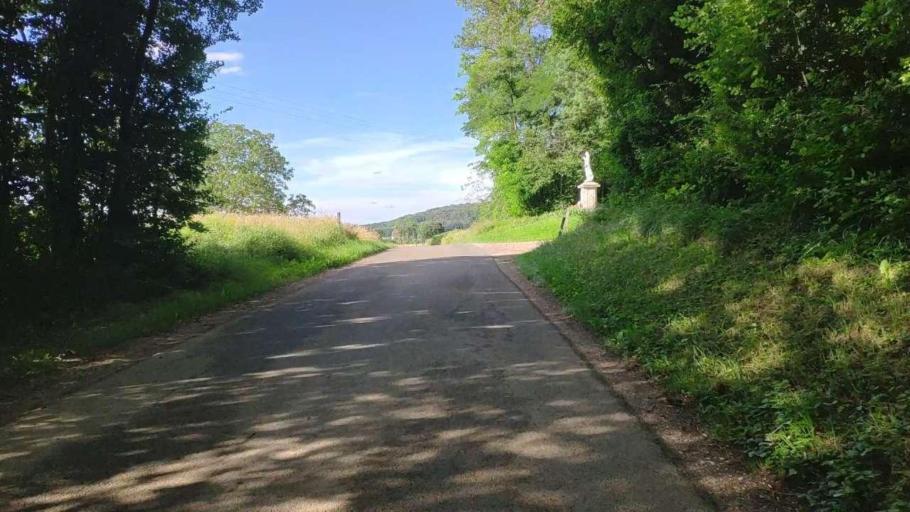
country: FR
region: Franche-Comte
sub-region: Departement du Jura
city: Bletterans
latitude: 46.7547
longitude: 5.5262
